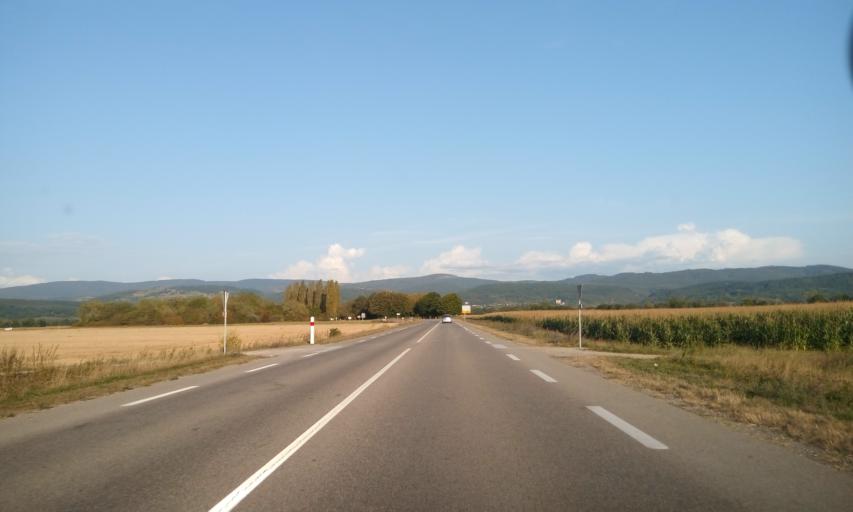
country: FR
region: Rhone-Alpes
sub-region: Departement de l'Ain
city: Ambronay
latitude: 46.0389
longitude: 5.3472
